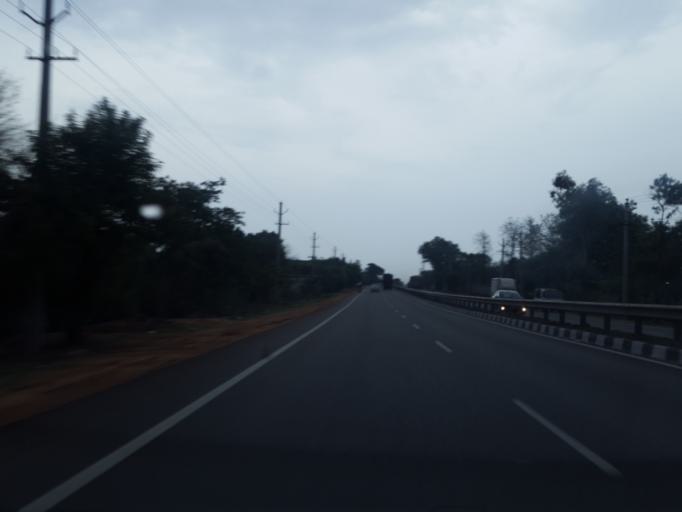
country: IN
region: Telangana
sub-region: Rangareddi
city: Sriramnagar
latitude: 17.1615
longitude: 78.2958
